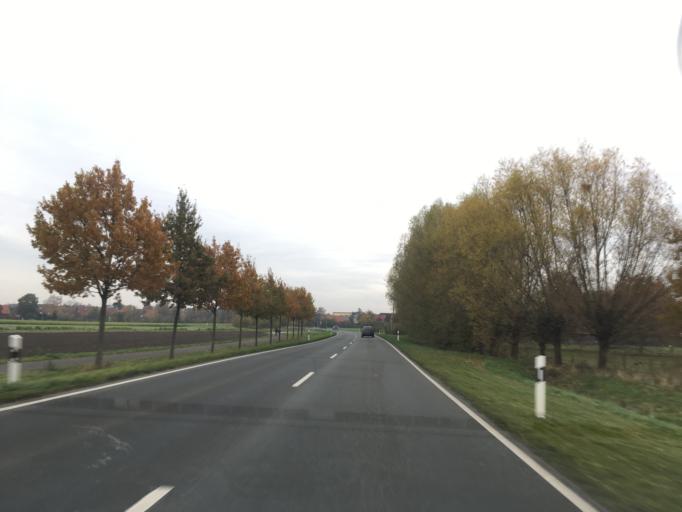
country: DE
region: North Rhine-Westphalia
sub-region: Regierungsbezirk Munster
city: Telgte
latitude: 51.9701
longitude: 7.7764
